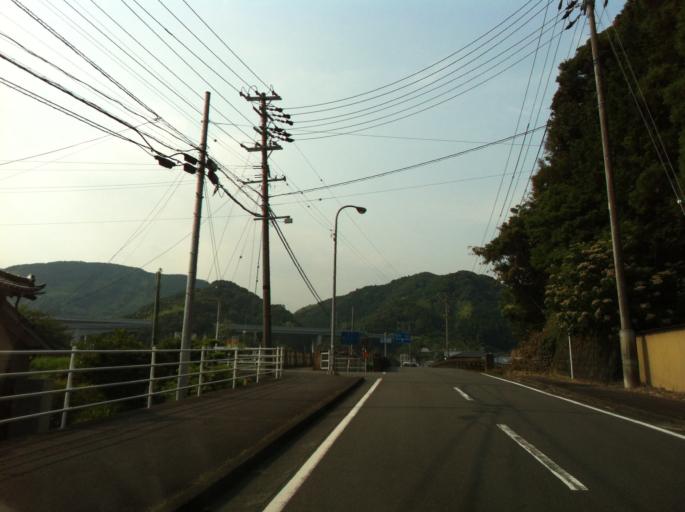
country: JP
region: Shizuoka
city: Fujieda
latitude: 34.9146
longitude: 138.2693
